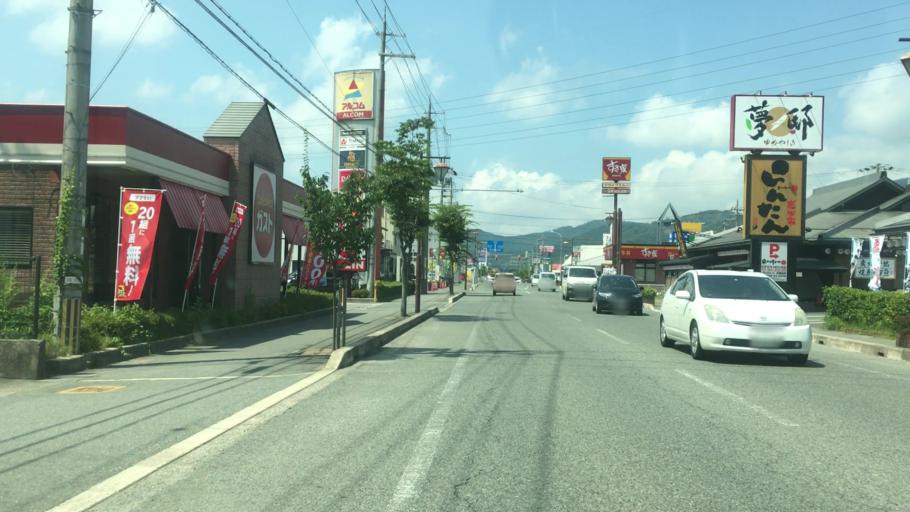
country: JP
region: Hyogo
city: Toyooka
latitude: 35.5525
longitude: 134.8155
